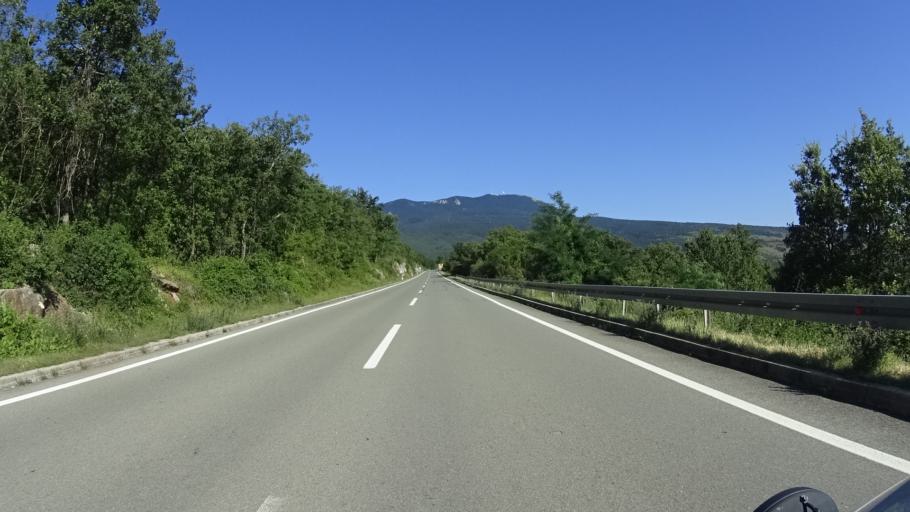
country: HR
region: Istarska
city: Lovran
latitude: 45.3252
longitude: 14.1437
